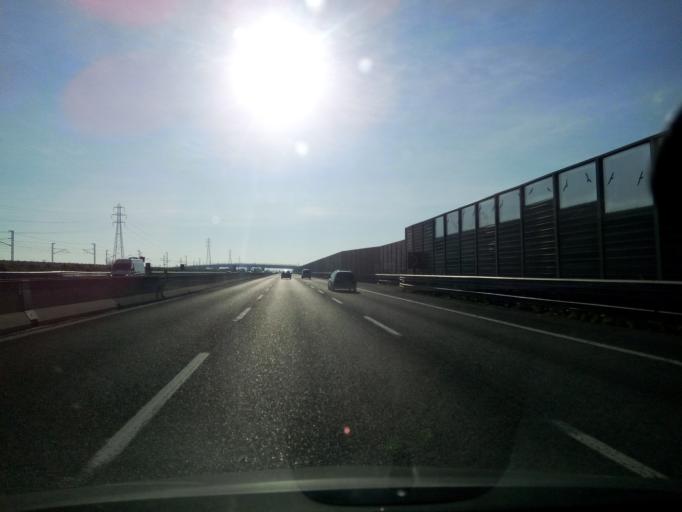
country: IT
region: Emilia-Romagna
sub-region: Provincia di Reggio Emilia
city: Massenzatico
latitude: 44.7155
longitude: 10.6941
